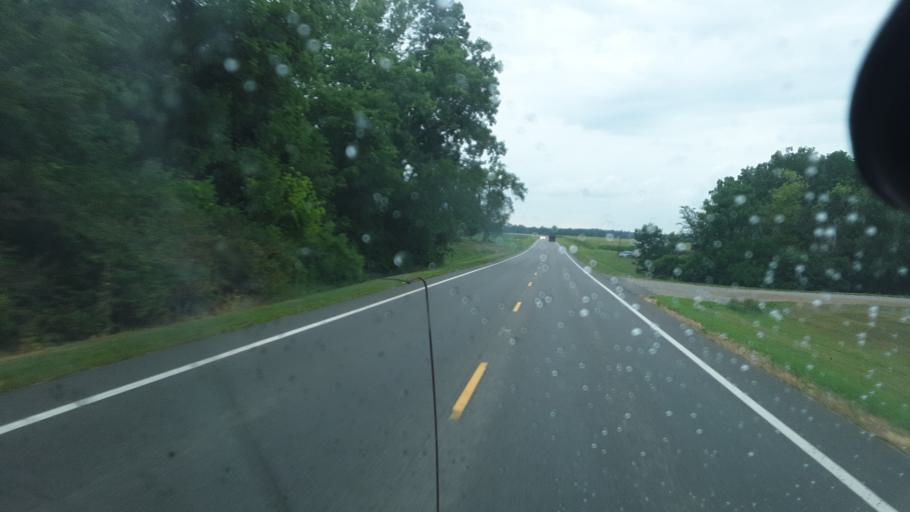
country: US
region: Ohio
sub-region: Williams County
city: Bryan
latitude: 41.4152
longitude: -84.6207
